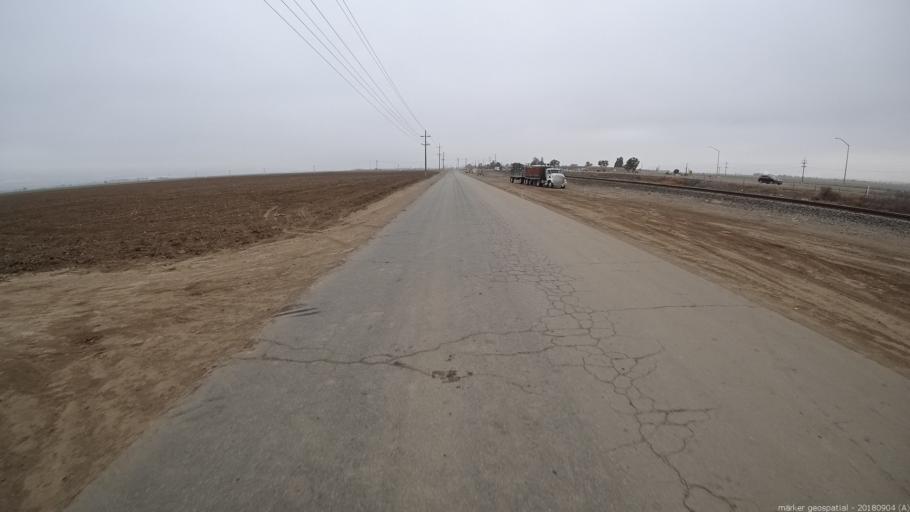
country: US
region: California
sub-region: Monterey County
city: Gonzales
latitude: 36.4886
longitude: -121.4245
